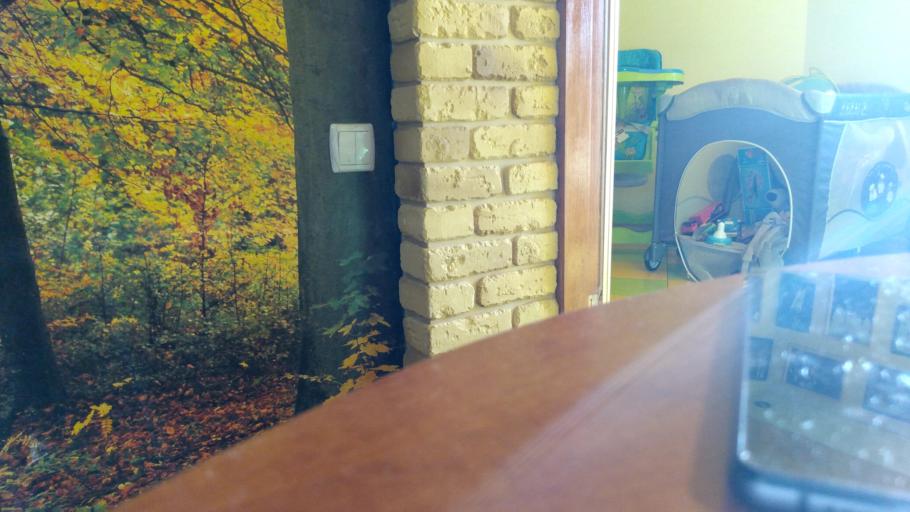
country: RU
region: Tverskaya
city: Likhoslavl'
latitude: 57.1244
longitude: 35.6549
